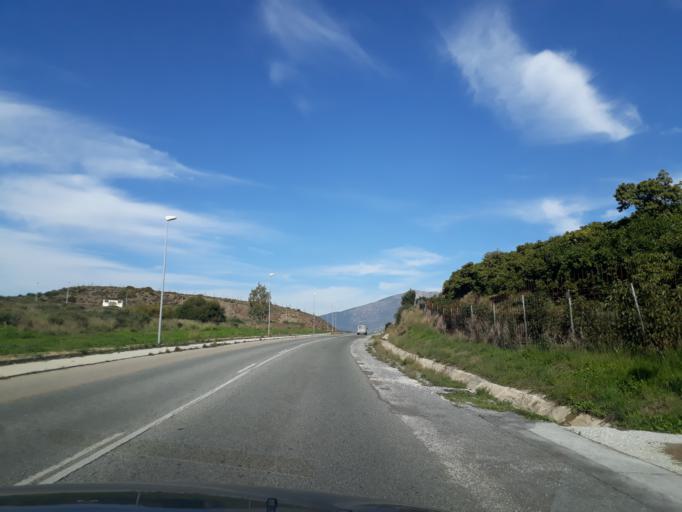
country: ES
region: Andalusia
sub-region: Provincia de Malaga
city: Fuengirola
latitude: 36.5294
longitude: -4.6860
